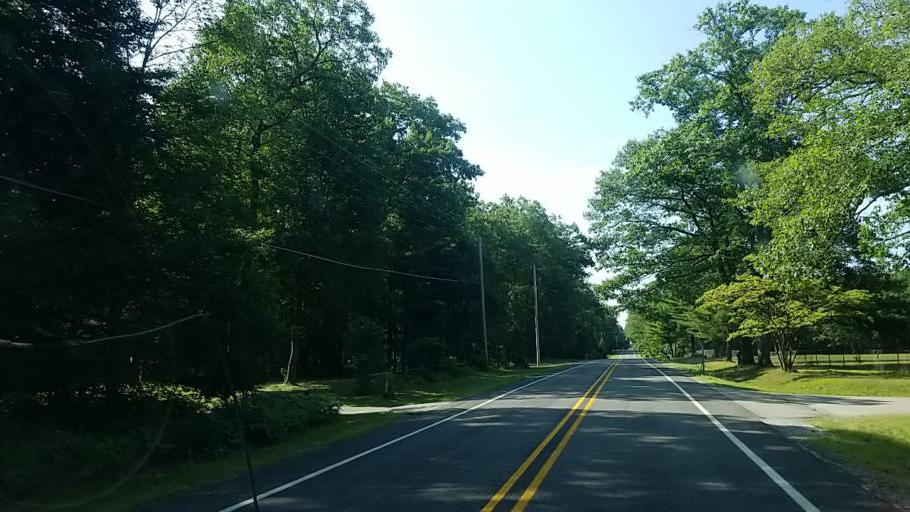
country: US
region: Michigan
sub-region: Muskegon County
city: Whitehall
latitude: 43.3408
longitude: -86.3765
